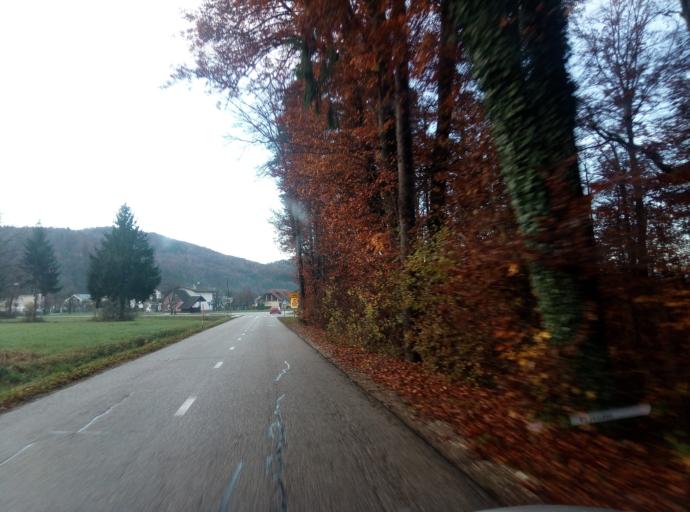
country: SI
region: Vodice
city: Vodice
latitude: 46.1645
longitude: 14.5172
